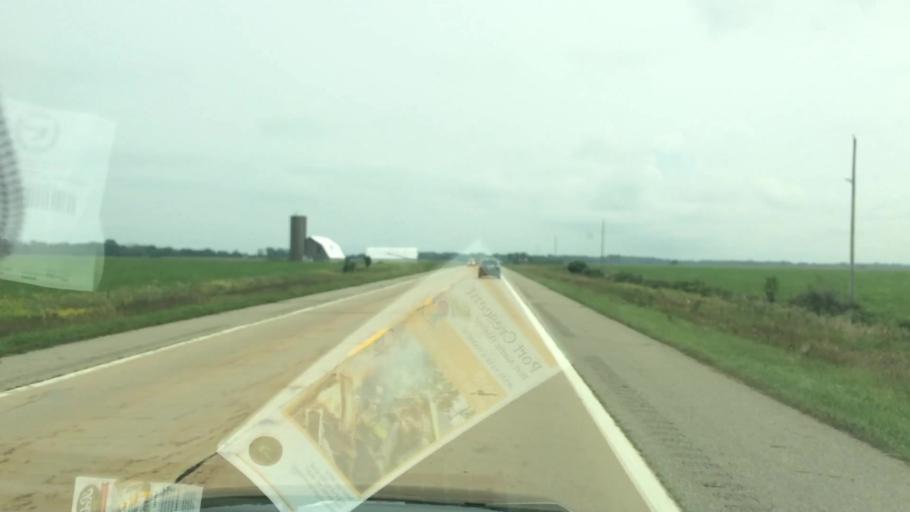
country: US
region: Michigan
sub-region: Huron County
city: Bad Axe
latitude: 44.0438
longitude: -82.9037
